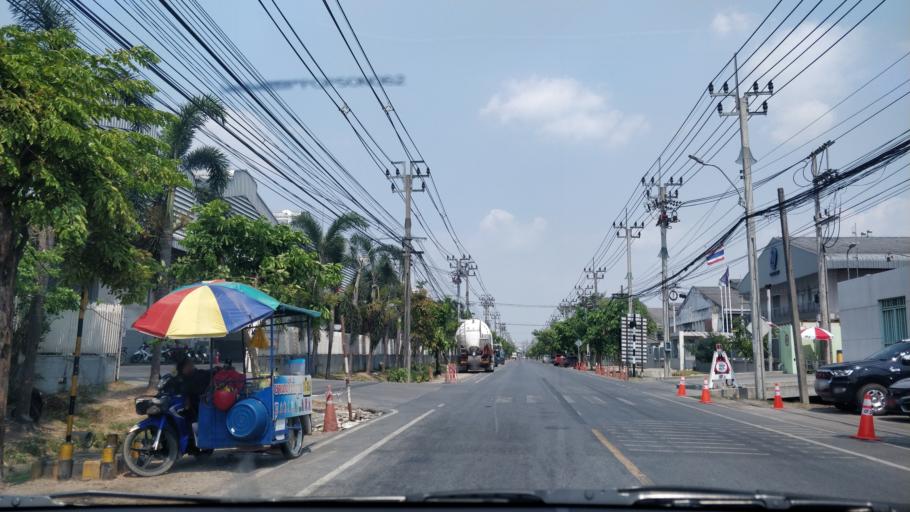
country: TH
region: Bangkok
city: Lat Krabang
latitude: 13.7713
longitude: 100.7858
